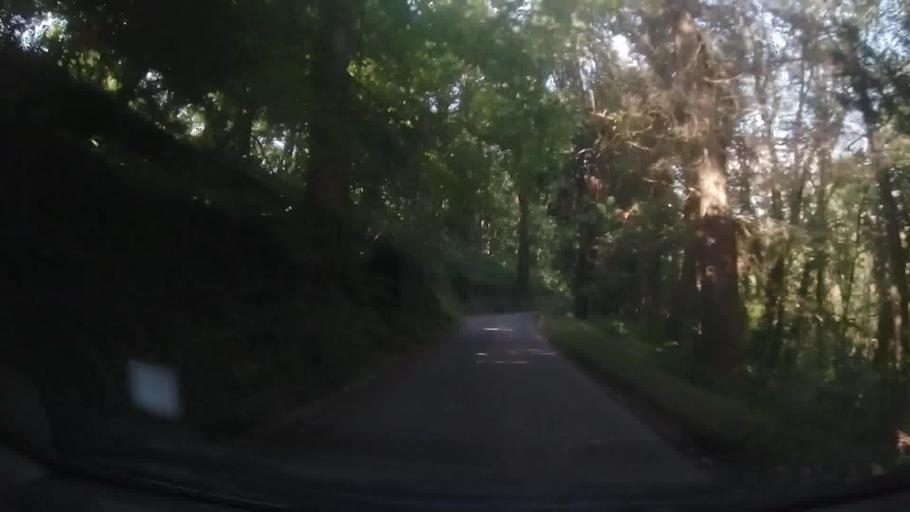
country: GB
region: Wales
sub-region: Pembrokeshire
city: Saundersfoot
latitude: 51.7429
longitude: -4.6750
